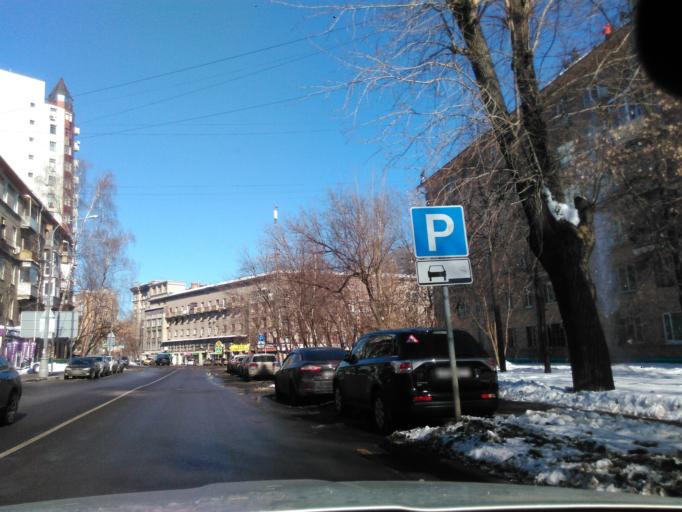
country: RU
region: Moskovskaya
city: Dorogomilovo
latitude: 55.7964
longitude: 37.5688
